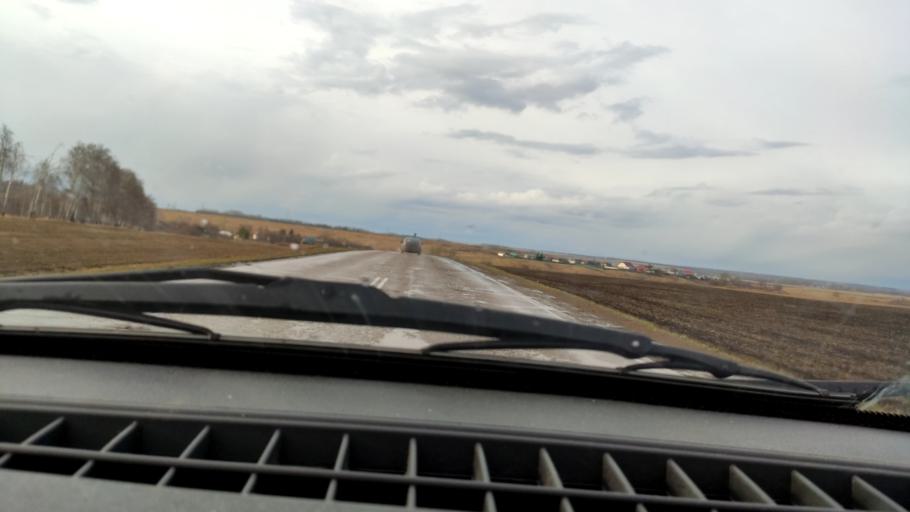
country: RU
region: Bashkortostan
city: Kushnarenkovo
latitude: 55.0888
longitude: 55.0628
